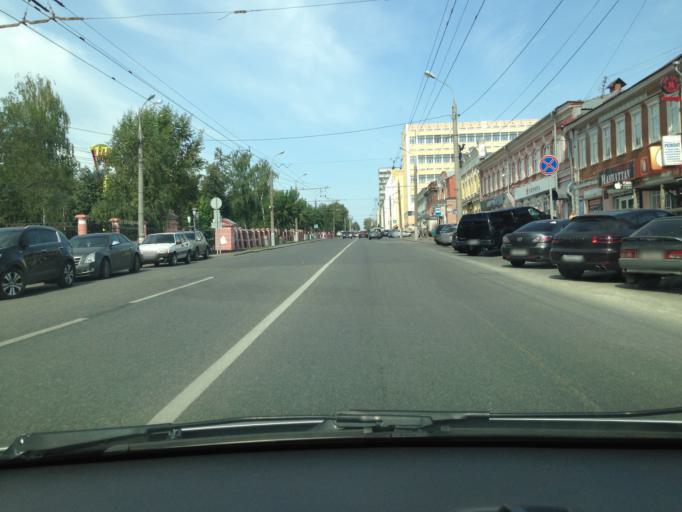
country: RU
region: Udmurtiya
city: Izhevsk
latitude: 56.8451
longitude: 53.2000
